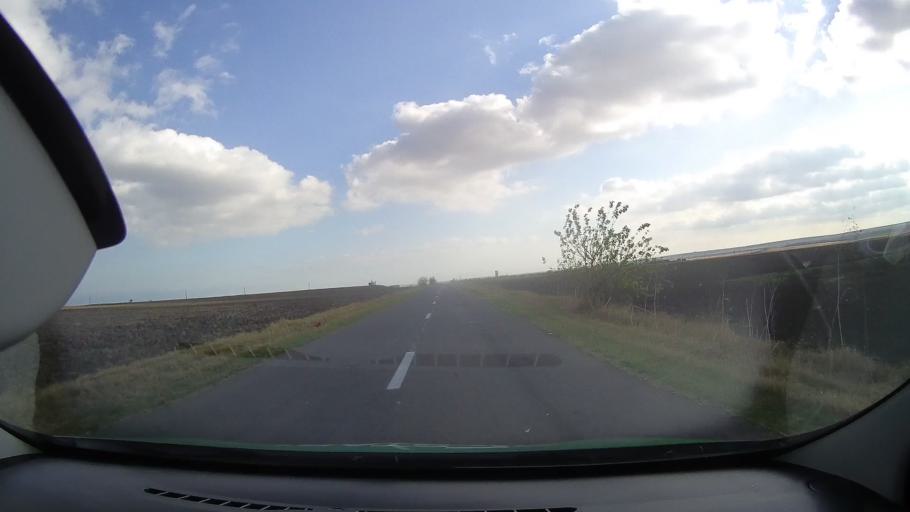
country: RO
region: Constanta
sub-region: Comuna Cogealac
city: Tariverde
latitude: 44.5533
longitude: 28.6225
